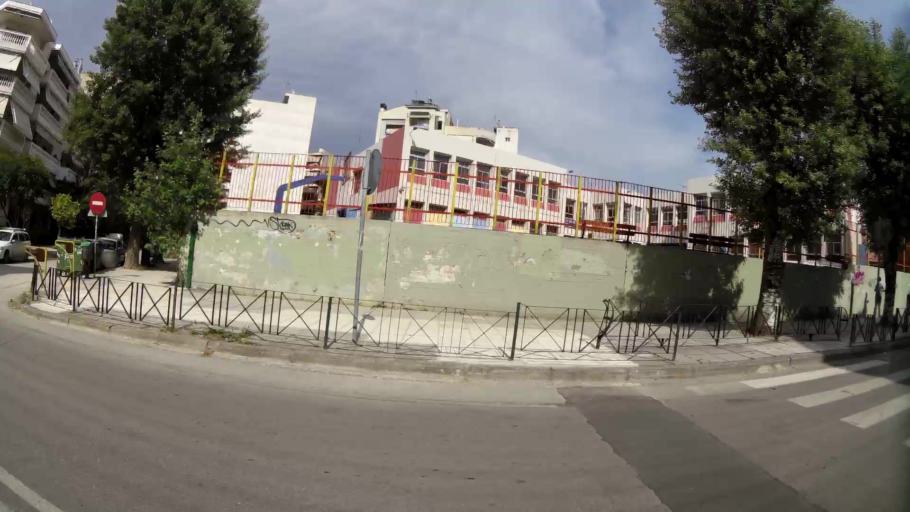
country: GR
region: Central Macedonia
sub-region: Nomos Thessalonikis
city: Kalamaria
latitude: 40.5828
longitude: 22.9663
